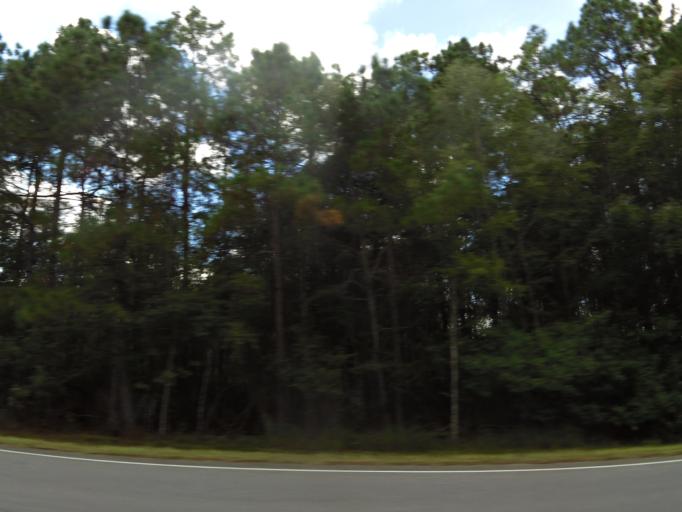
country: US
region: Georgia
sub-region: Brantley County
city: Nahunta
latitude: 31.0244
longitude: -82.0233
